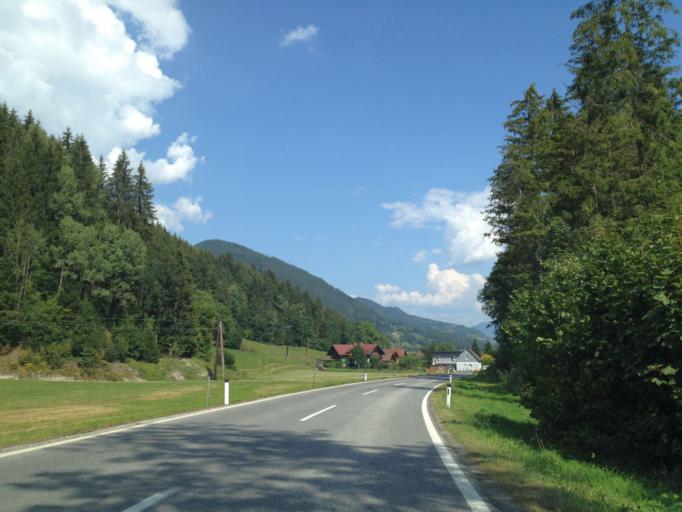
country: AT
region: Styria
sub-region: Politischer Bezirk Liezen
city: Haus im Ennstal
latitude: 47.4254
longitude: 13.7681
